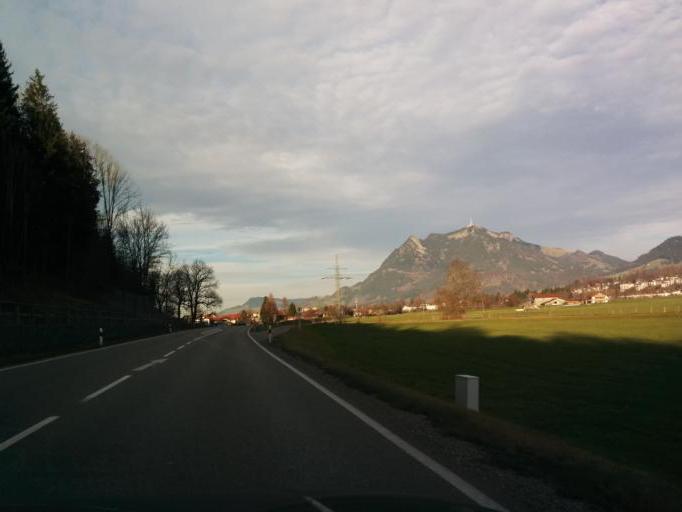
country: DE
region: Bavaria
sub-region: Swabia
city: Sonthofen
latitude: 47.4986
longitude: 10.2659
